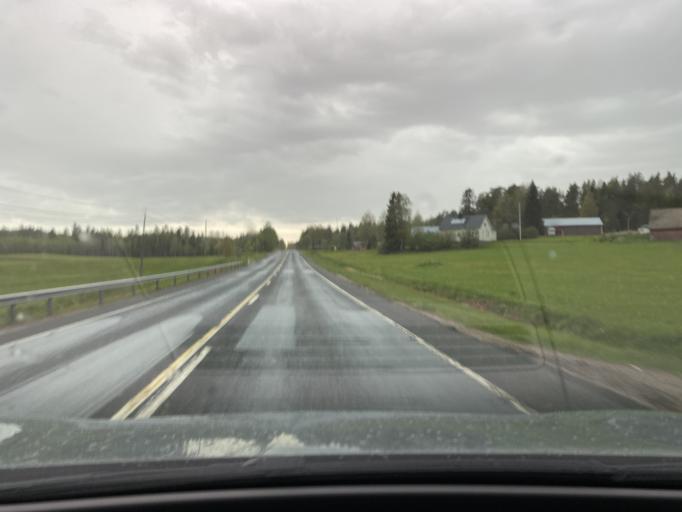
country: FI
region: Varsinais-Suomi
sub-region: Salo
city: Suomusjaervi
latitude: 60.3745
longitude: 23.6200
